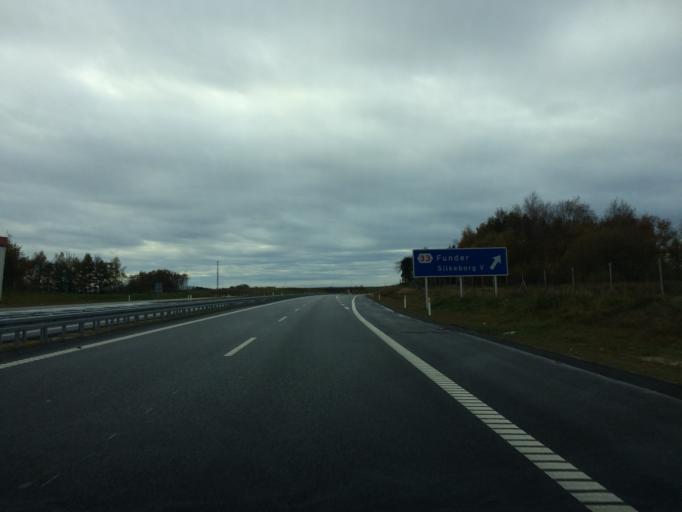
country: DK
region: Central Jutland
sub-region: Silkeborg Kommune
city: Silkeborg
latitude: 56.1565
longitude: 9.4603
